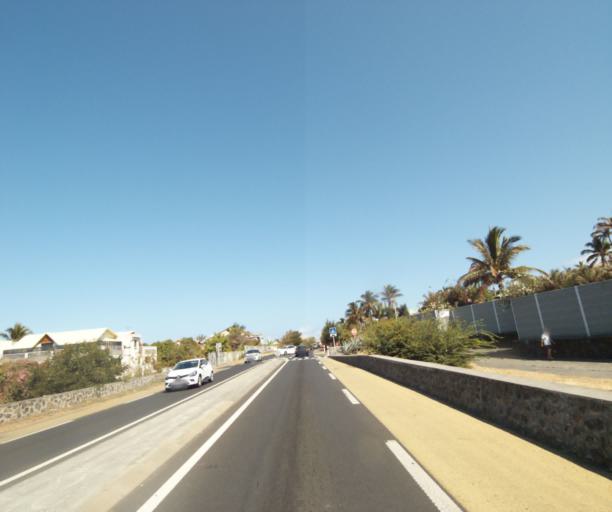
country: RE
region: Reunion
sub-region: Reunion
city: Trois-Bassins
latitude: -21.1065
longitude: 55.2520
